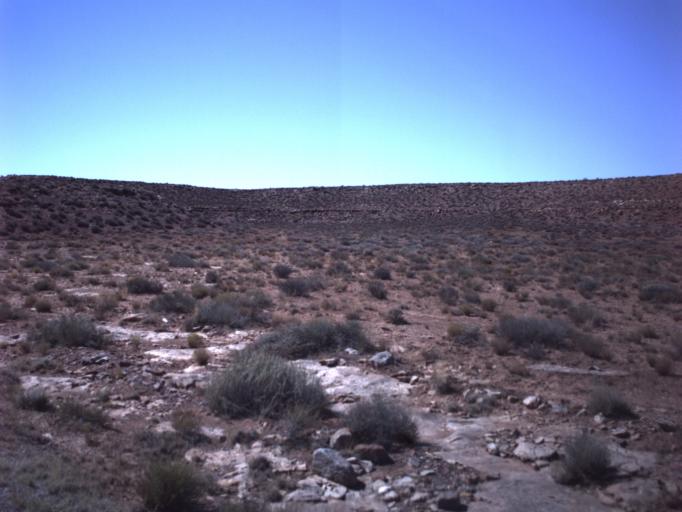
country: US
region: Arizona
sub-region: Navajo County
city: Kayenta
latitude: 37.1955
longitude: -109.9063
